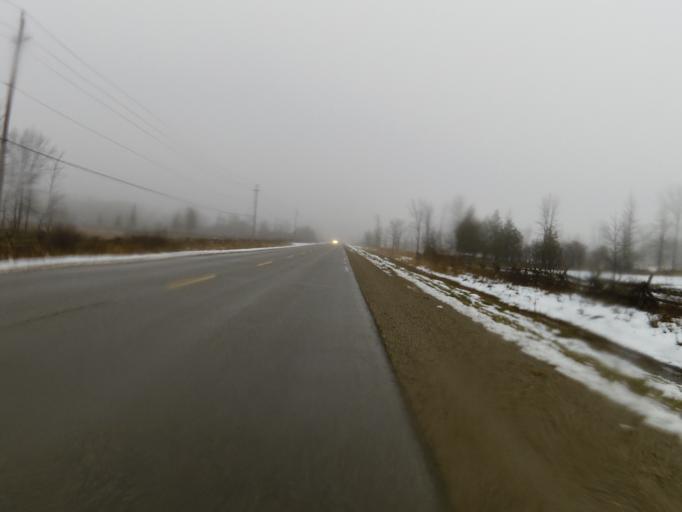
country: CA
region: Ontario
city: Perth
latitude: 44.8315
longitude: -76.3863
